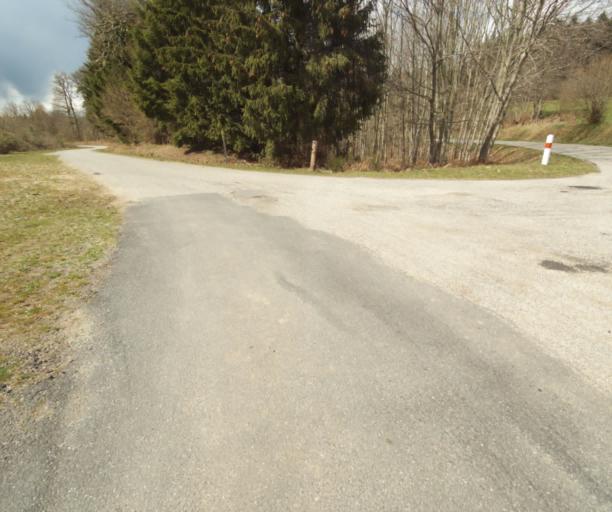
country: FR
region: Limousin
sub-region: Departement de la Correze
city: Correze
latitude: 45.2717
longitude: 1.9768
